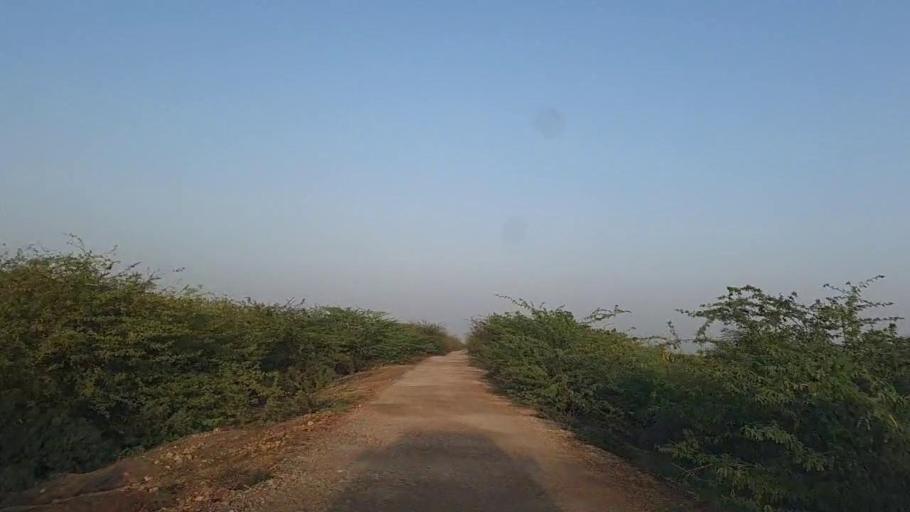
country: PK
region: Sindh
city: Naukot
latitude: 24.6973
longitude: 69.2507
